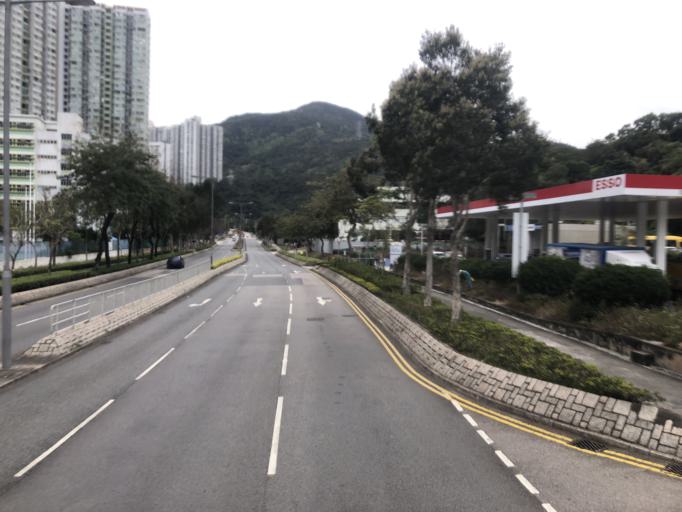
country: HK
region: Sai Kung
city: Sai Kung
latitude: 22.3272
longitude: 114.2549
